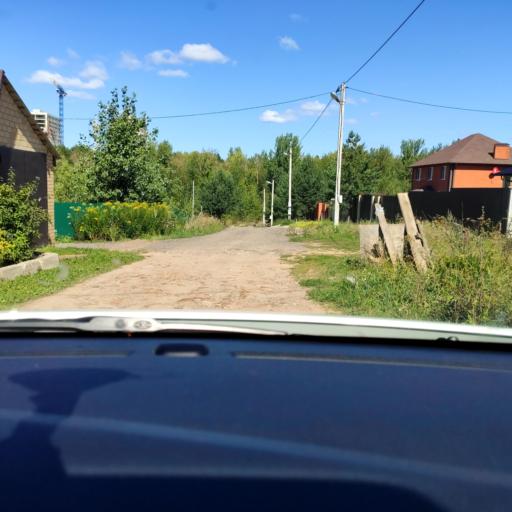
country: RU
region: Tatarstan
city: Vysokaya Gora
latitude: 55.7846
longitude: 49.2586
